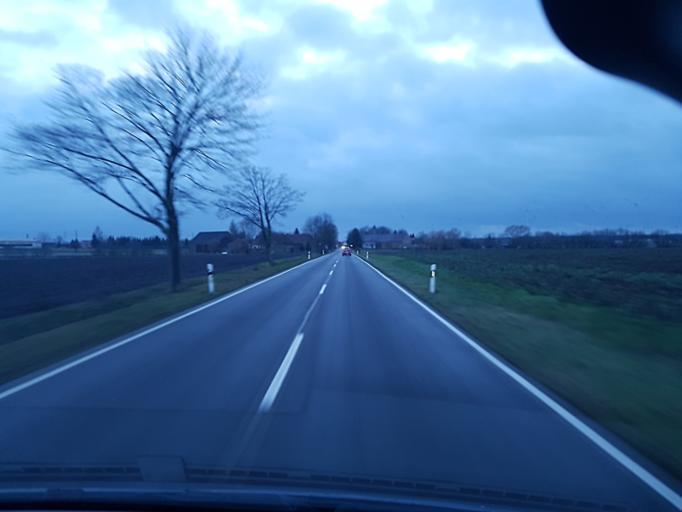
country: DE
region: Brandenburg
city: Bronkow
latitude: 51.6442
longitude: 13.8658
